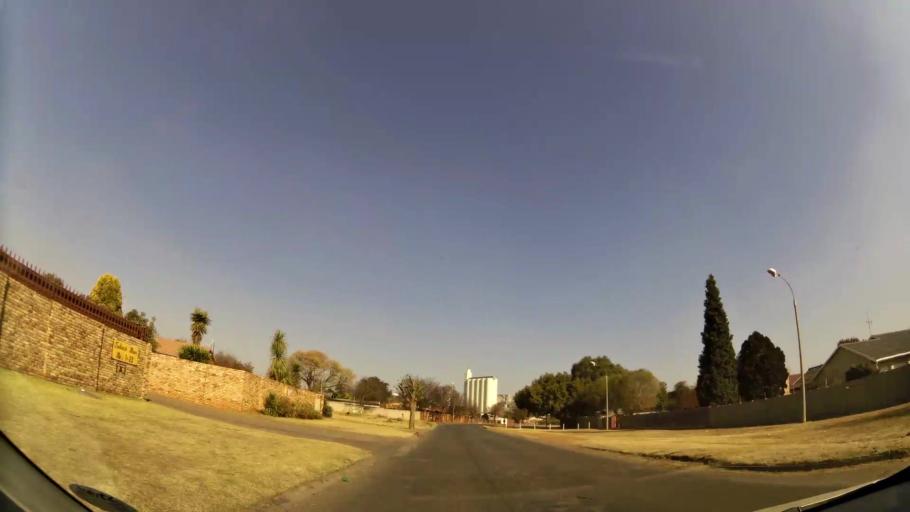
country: ZA
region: Gauteng
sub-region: West Rand District Municipality
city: Randfontein
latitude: -26.1804
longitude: 27.6924
